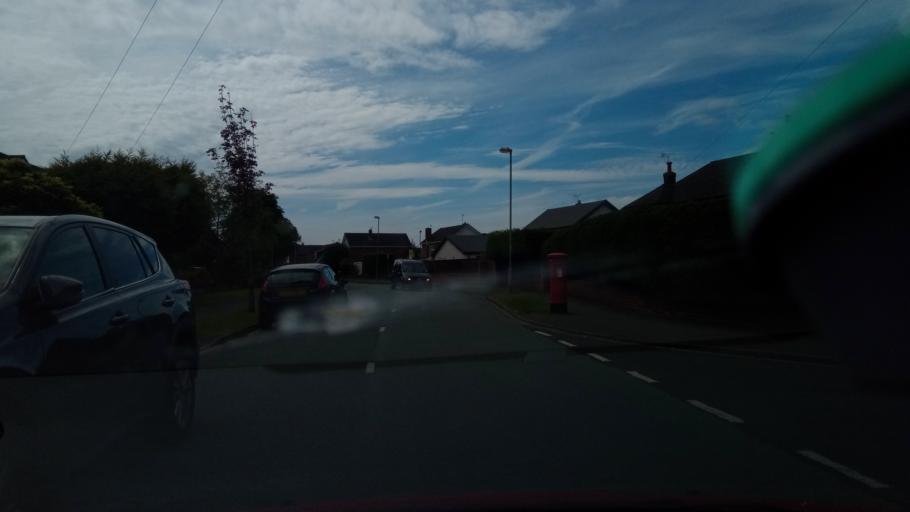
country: GB
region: England
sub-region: Sefton
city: Formby
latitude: 53.5513
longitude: -3.0775
